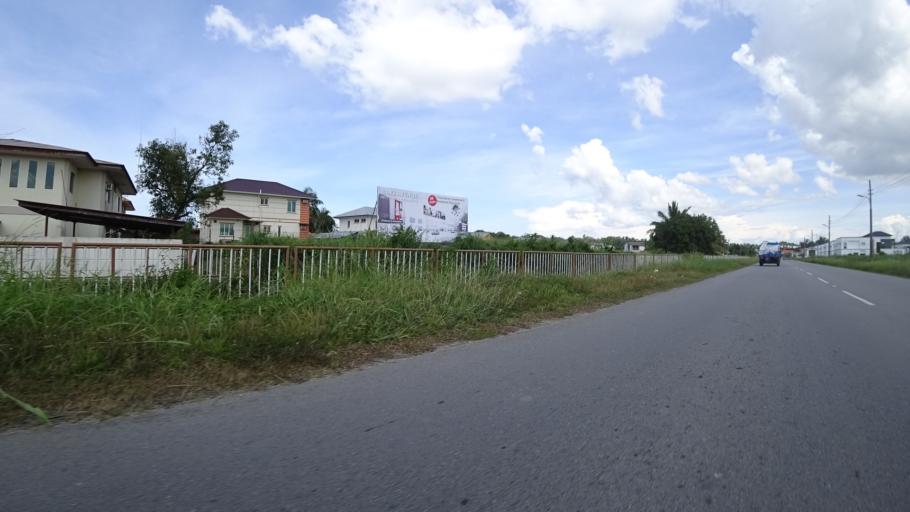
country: BN
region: Brunei and Muara
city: Bandar Seri Begawan
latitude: 4.8841
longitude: 114.8514
